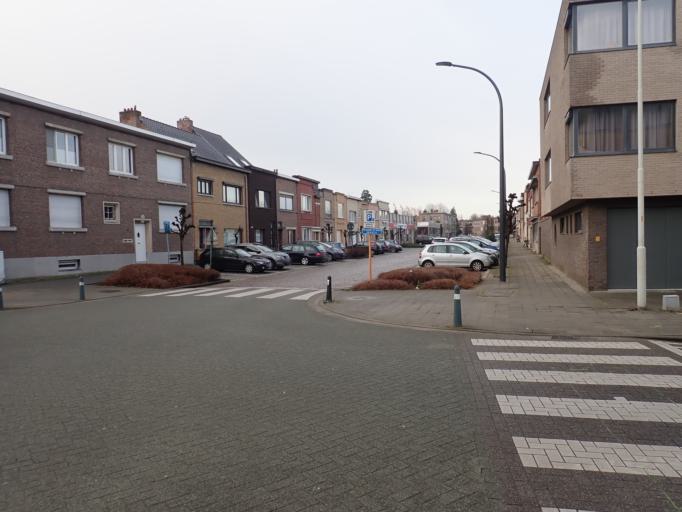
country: BE
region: Flanders
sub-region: Provincie Antwerpen
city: Lier
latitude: 51.1383
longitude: 4.5627
